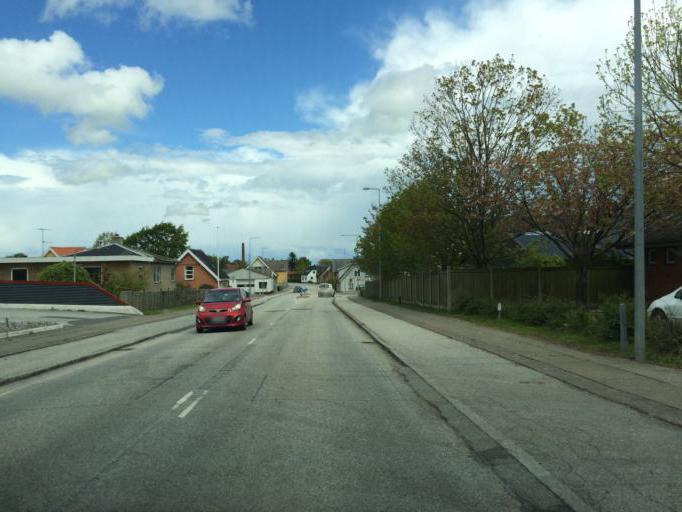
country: DK
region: North Denmark
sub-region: Vesthimmerland Kommune
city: Farso
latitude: 56.7643
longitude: 9.3380
